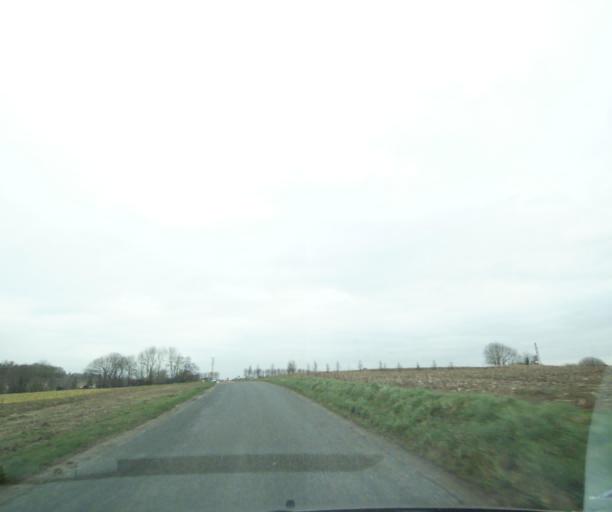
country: FR
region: Picardie
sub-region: Departement de l'Oise
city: Noyon
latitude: 49.5704
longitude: 2.9706
